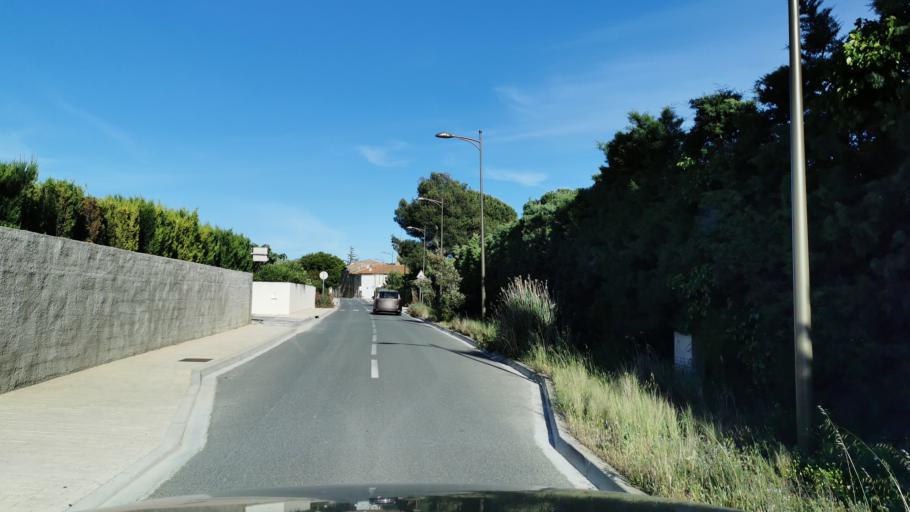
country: FR
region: Languedoc-Roussillon
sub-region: Departement de l'Aude
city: Nevian
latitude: 43.2123
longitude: 2.8994
